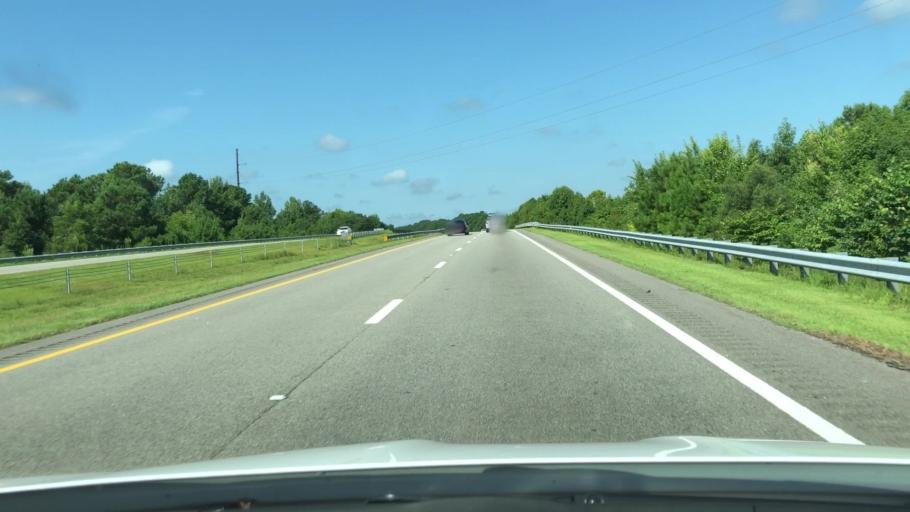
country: US
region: North Carolina
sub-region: Chowan County
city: Edenton
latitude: 36.0899
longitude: -76.5811
